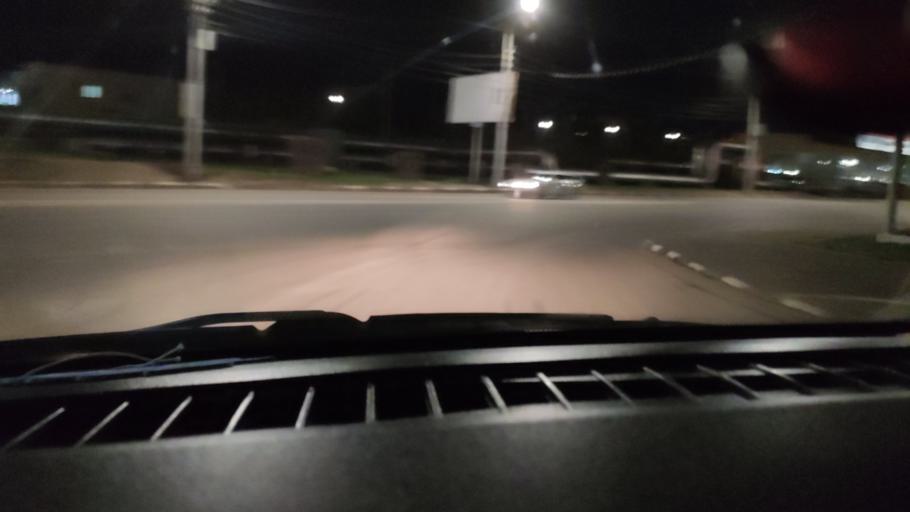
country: RU
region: Saratov
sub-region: Saratovskiy Rayon
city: Saratov
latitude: 51.5680
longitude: 45.9979
